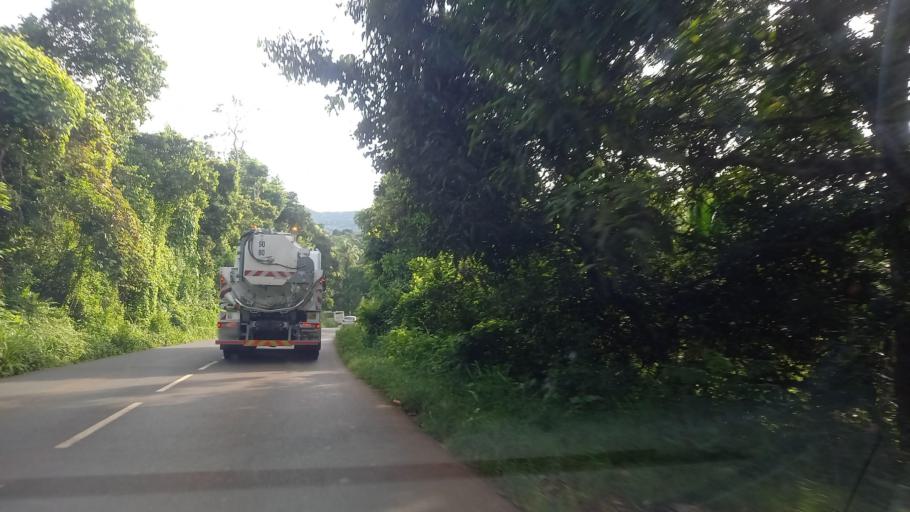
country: YT
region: Chiconi
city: Chiconi
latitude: -12.8182
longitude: 45.1296
